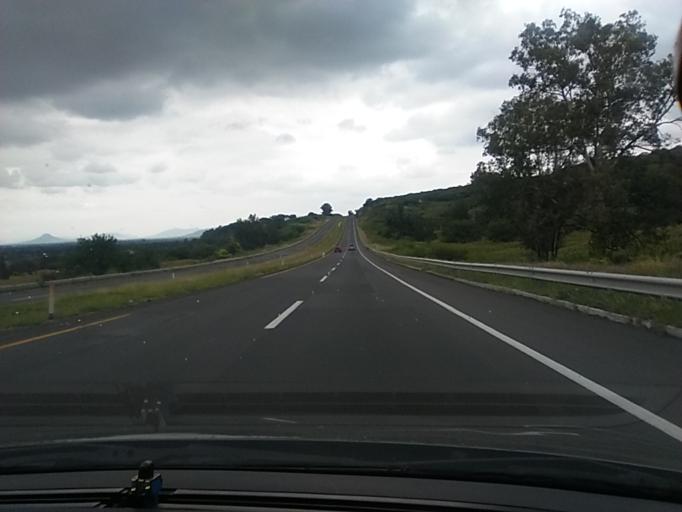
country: MX
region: Jalisco
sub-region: Poncitlan
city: Santa Cruz el Grande
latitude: 20.4424
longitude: -102.8265
